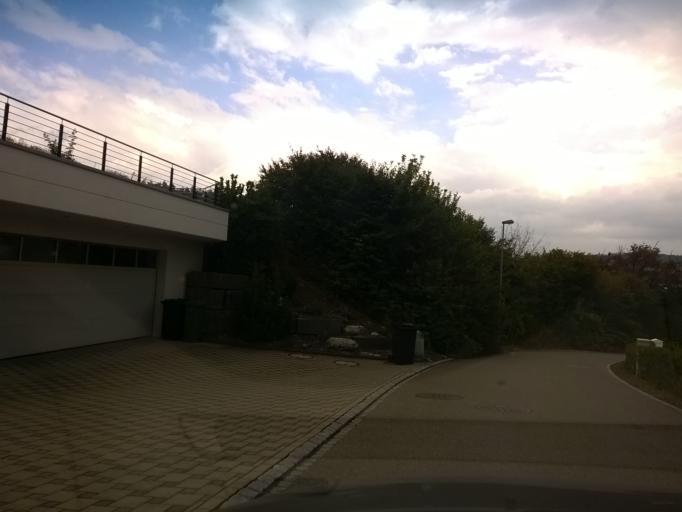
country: CH
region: Zurich
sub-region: Bezirk Buelach
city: Embrach / Embrach (Dorfkern)
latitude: 47.5049
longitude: 8.6028
